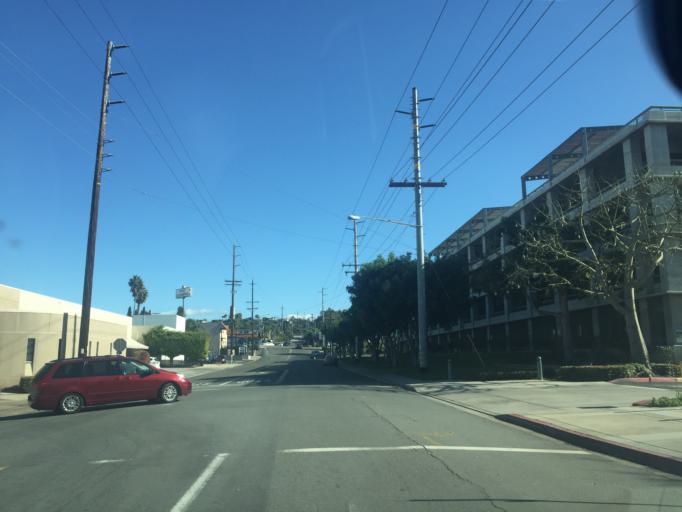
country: US
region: California
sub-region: San Diego County
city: La Mesa
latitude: 32.7877
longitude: -117.0998
